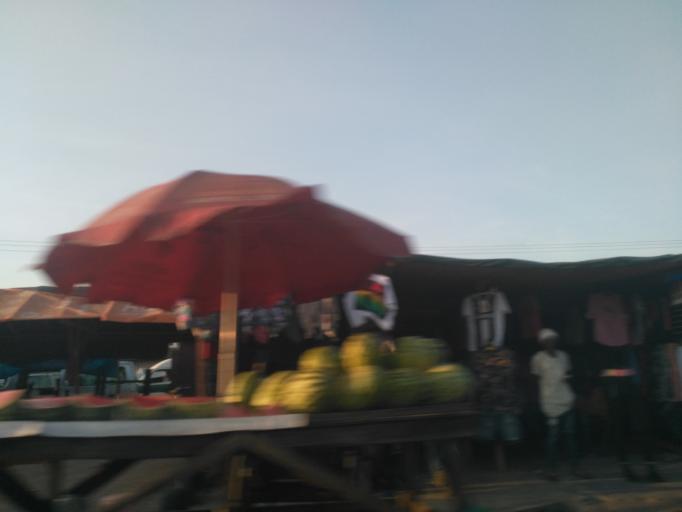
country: TZ
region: Dar es Salaam
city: Dar es Salaam
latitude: -6.9153
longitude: 39.2710
